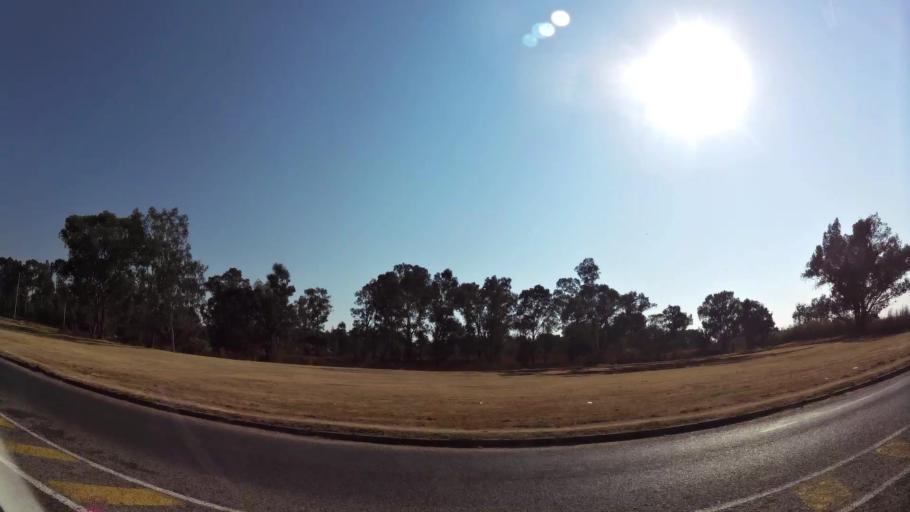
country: ZA
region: Gauteng
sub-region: Ekurhuleni Metropolitan Municipality
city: Boksburg
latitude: -26.2183
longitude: 28.2543
